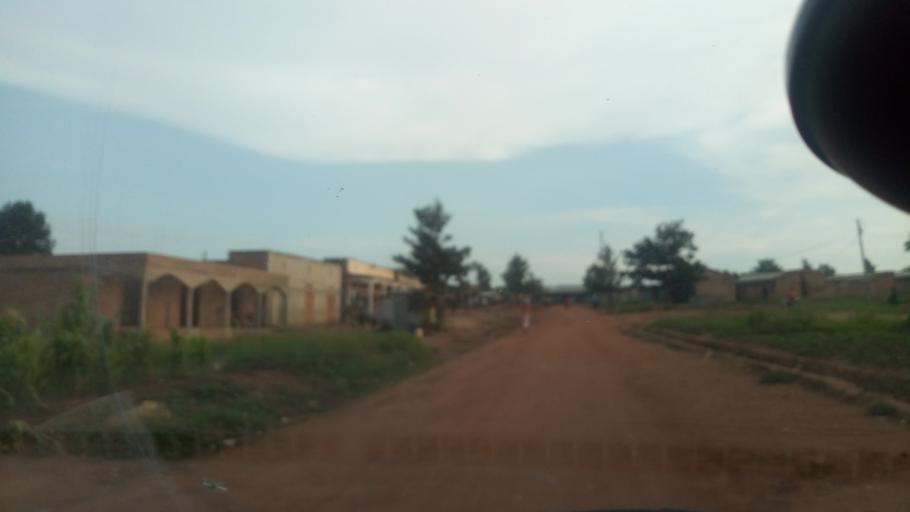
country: UG
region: Western Region
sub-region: Kiryandongo District
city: Kiryandongo
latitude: 1.8126
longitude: 32.0111
